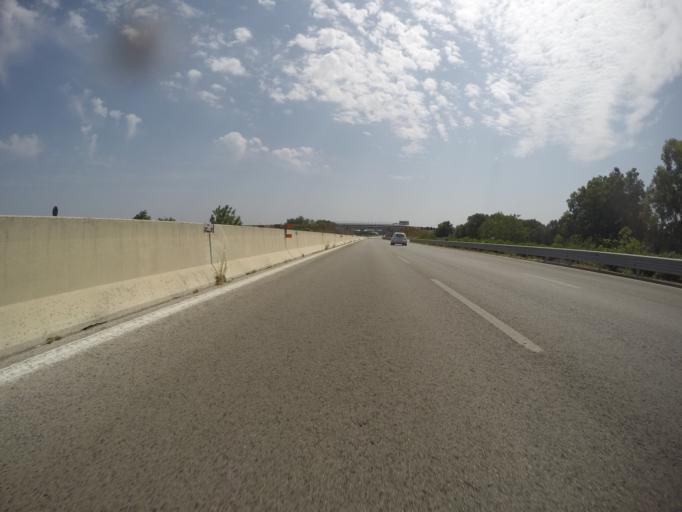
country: IT
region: Apulia
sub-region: Provincia di Brindisi
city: Mesagne
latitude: 40.5673
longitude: 17.7838
